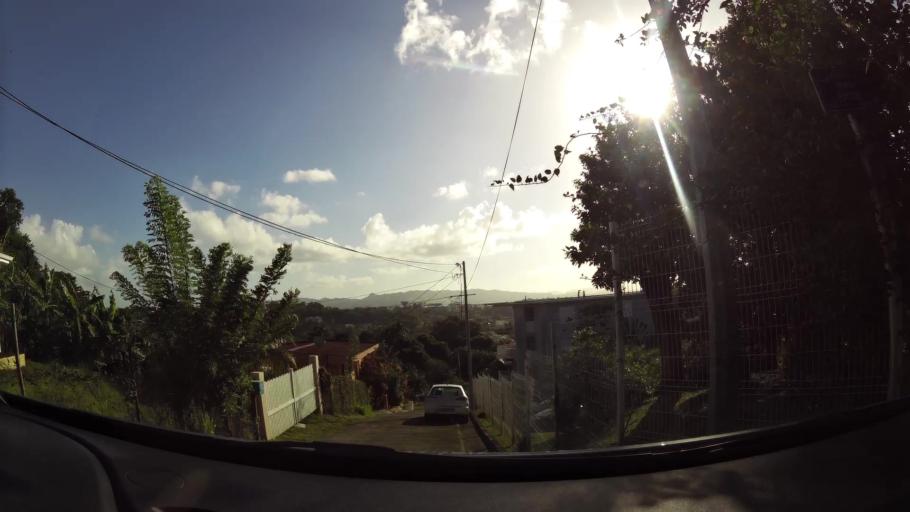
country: MQ
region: Martinique
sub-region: Martinique
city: Le Lamentin
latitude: 14.6298
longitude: -61.0286
